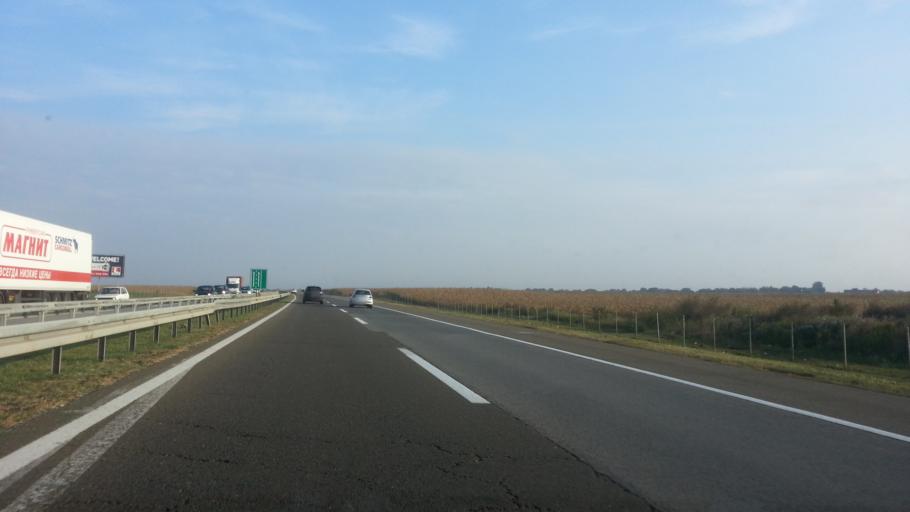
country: RS
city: Novi Banovci
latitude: 44.9188
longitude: 20.3048
